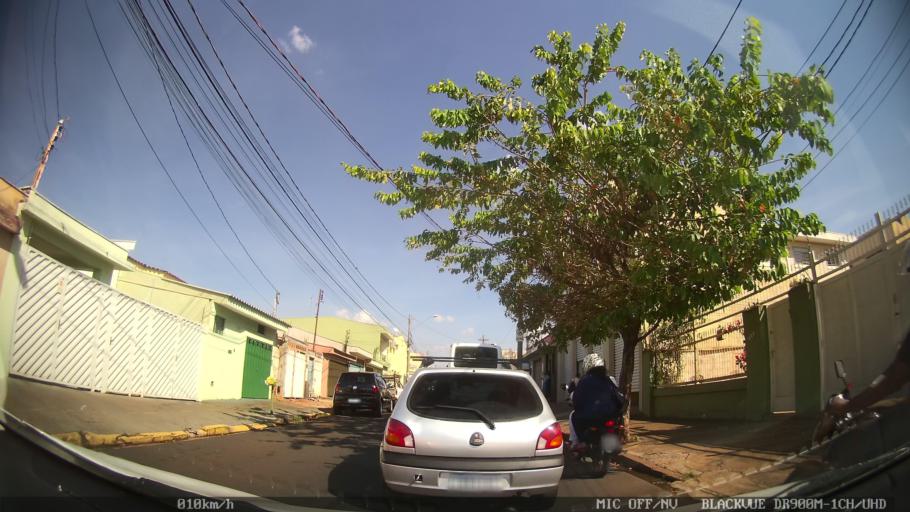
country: BR
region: Sao Paulo
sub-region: Ribeirao Preto
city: Ribeirao Preto
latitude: -21.1849
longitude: -47.8262
